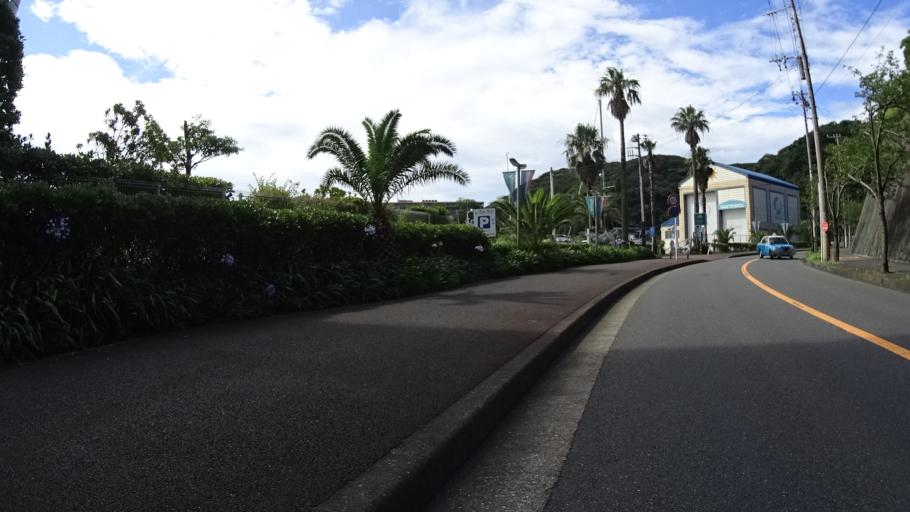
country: JP
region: Kanagawa
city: Yokosuka
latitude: 35.2356
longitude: 139.7226
